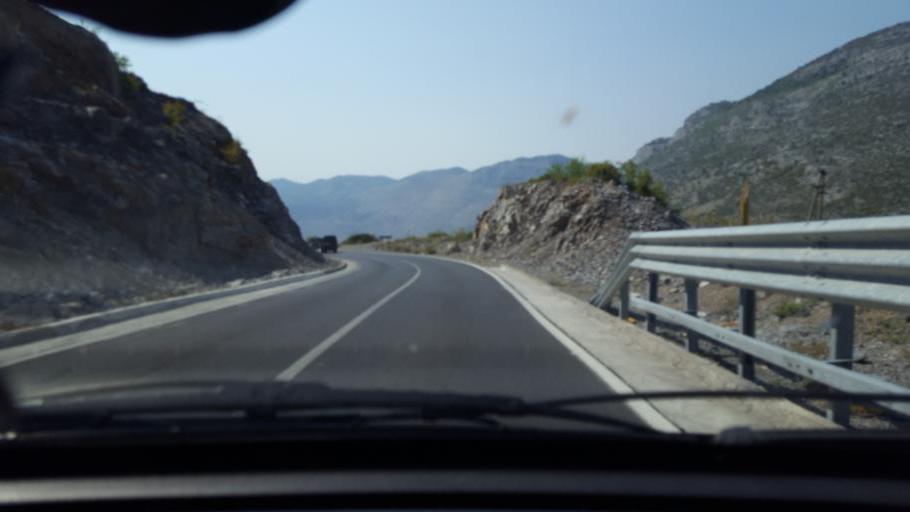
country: AL
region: Shkoder
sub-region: Rrethi i Malesia e Madhe
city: Kastrat
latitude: 42.3753
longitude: 19.4857
